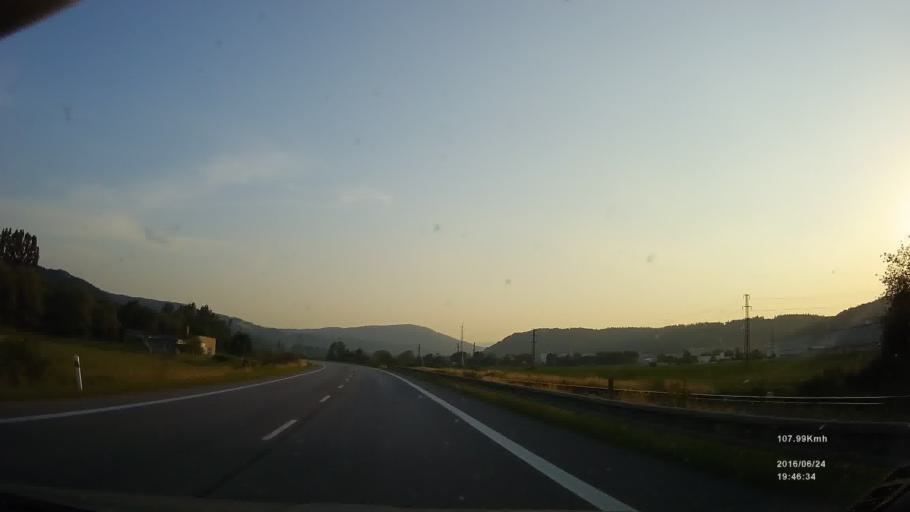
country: SK
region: Banskobystricky
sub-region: Okres Banska Bystrica
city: Banska Bystrica
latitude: 48.7557
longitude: 19.2603
